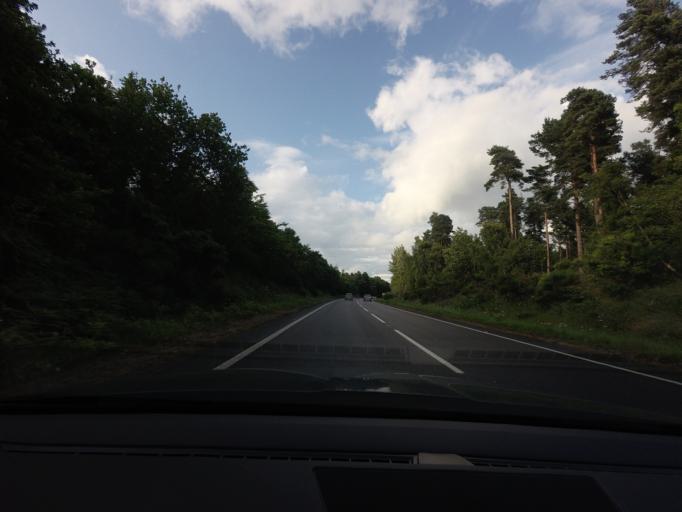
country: GB
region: Scotland
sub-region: Highland
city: Fortrose
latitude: 57.5258
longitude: -4.0596
